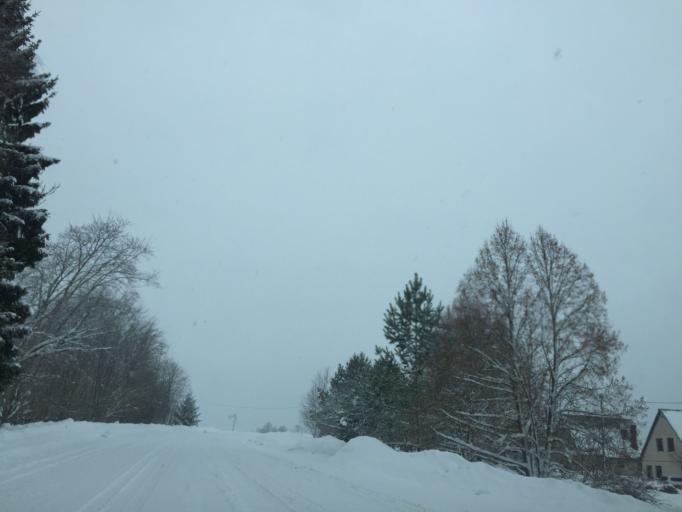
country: LV
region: Amatas Novads
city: Drabesi
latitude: 57.1679
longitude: 25.3229
